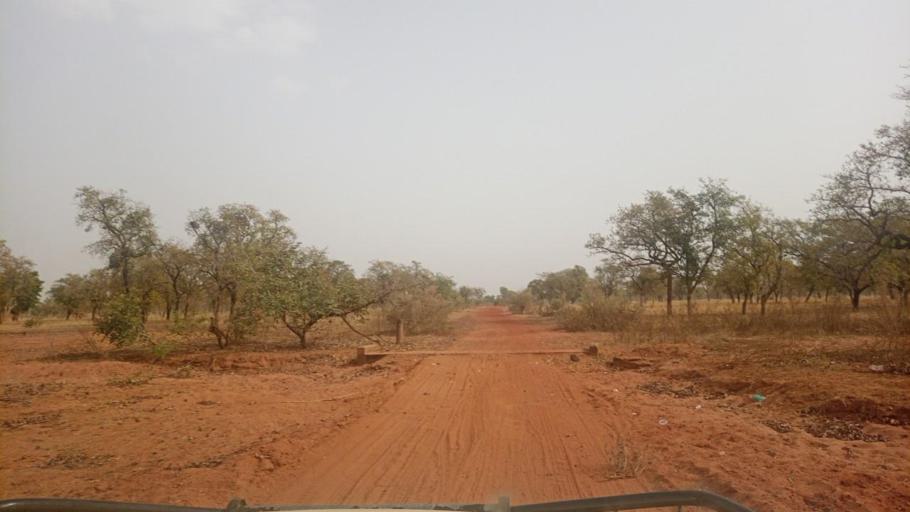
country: BF
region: Boucle du Mouhoun
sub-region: Province des Banwa
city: Salanso
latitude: 12.1041
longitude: -4.3348
